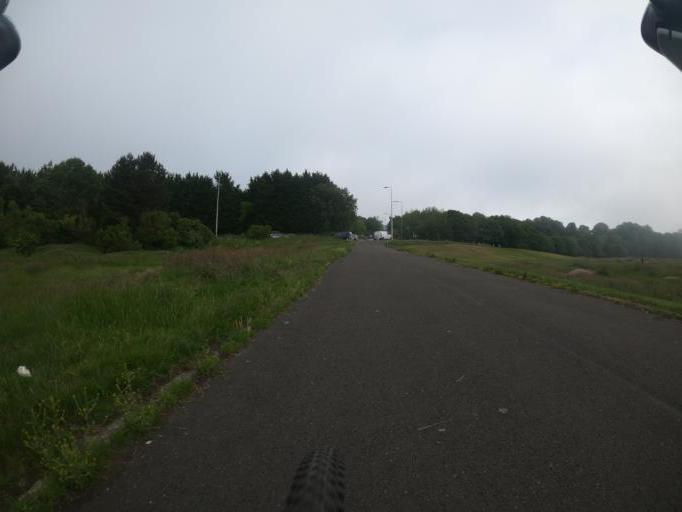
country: GB
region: Scotland
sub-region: Edinburgh
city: Edinburgh
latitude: 55.9821
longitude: -3.2525
